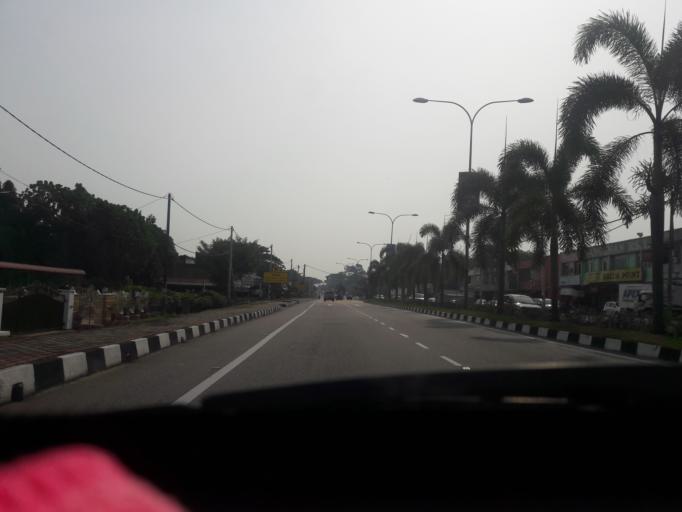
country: MY
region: Kedah
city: Kulim
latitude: 5.3620
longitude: 100.5479
